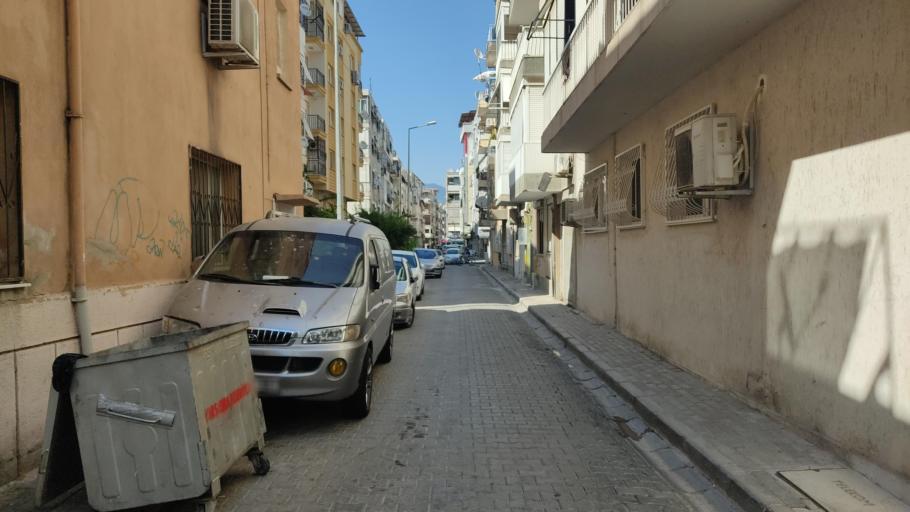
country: TR
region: Izmir
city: Karsiyaka
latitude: 38.4579
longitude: 27.1238
